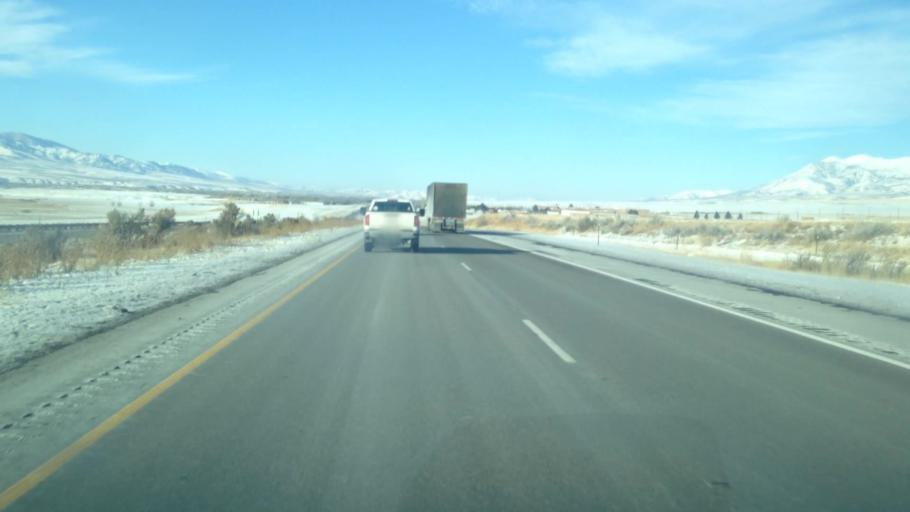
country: US
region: Idaho
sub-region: Oneida County
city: Malad City
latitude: 42.5681
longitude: -112.1796
